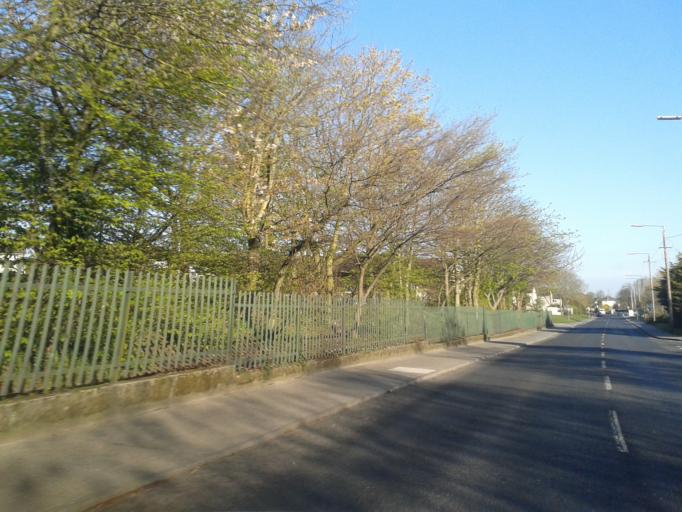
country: IE
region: Leinster
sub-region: Fingal County
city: Swords
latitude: 53.4627
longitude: -6.2326
